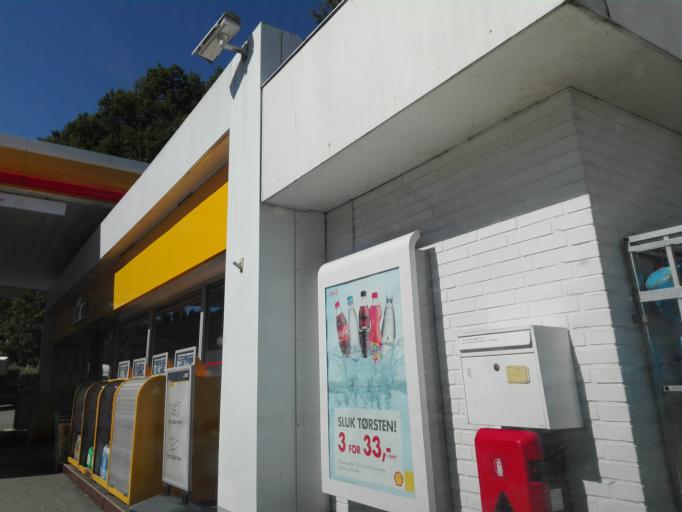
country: DK
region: North Denmark
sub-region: Mariagerfjord Kommune
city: Hadsund
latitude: 56.7177
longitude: 10.1109
